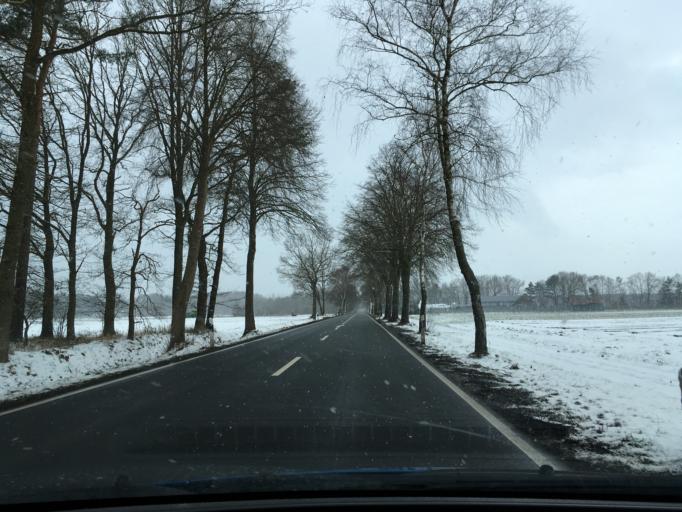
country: DE
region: Lower Saxony
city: Vierhofen
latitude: 53.2913
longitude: 10.1986
